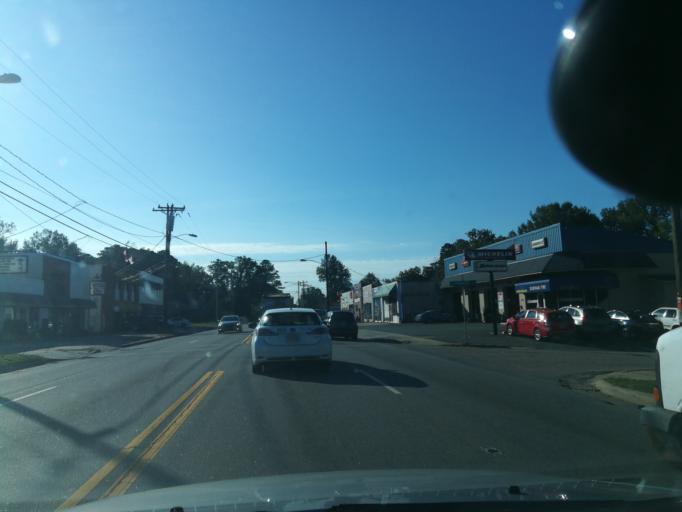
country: US
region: North Carolina
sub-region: Durham County
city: Durham
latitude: 36.0284
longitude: -78.8901
